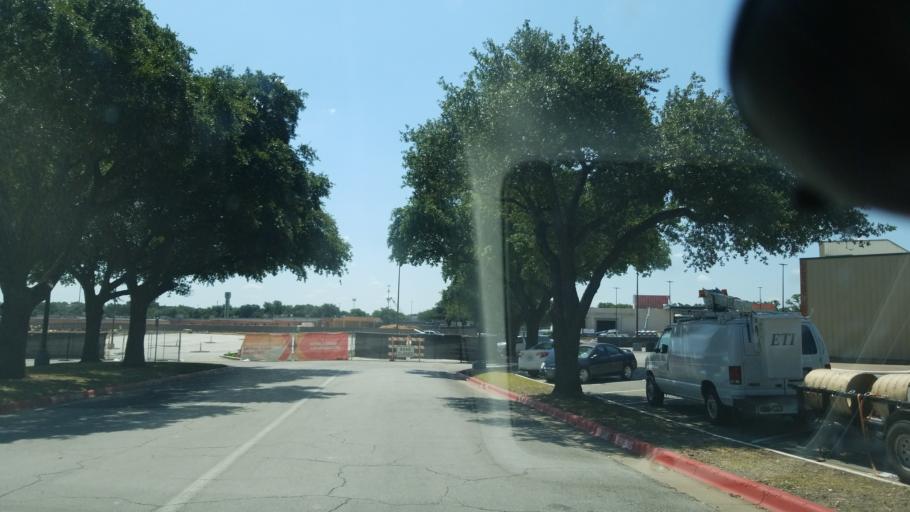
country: US
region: Texas
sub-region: Dallas County
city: Cockrell Hill
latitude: 32.7232
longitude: -96.8350
